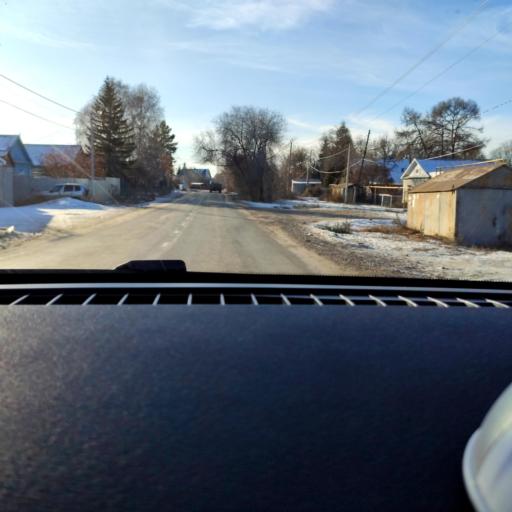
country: RU
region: Samara
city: Novokuybyshevsk
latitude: 53.1193
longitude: 49.8940
